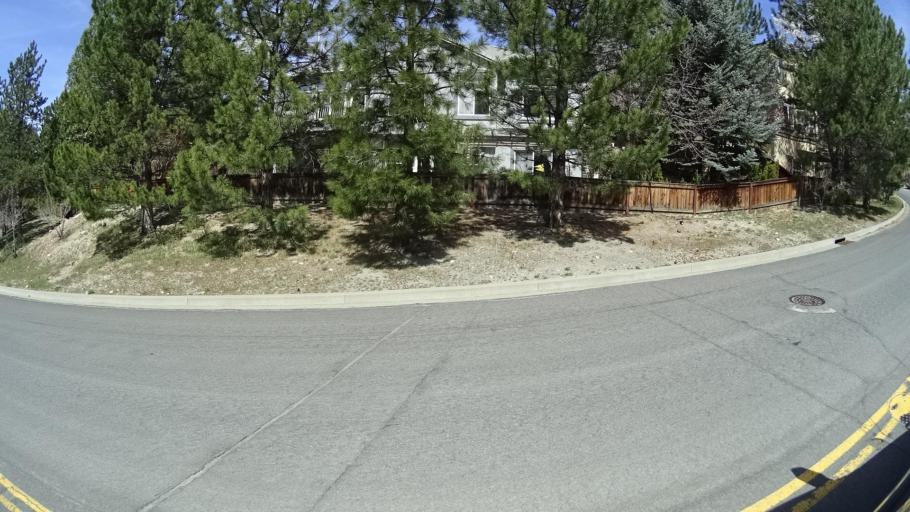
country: US
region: Nevada
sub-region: Washoe County
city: Reno
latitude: 39.4829
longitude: -119.8621
